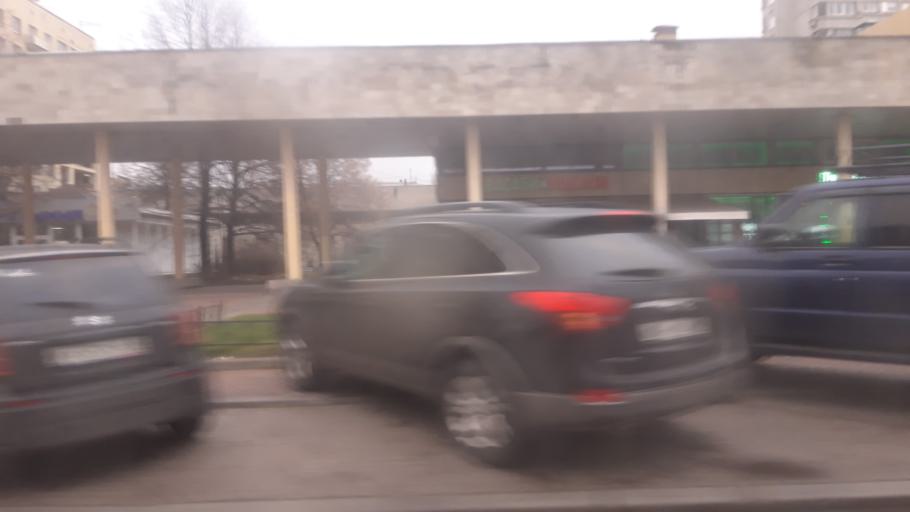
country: RU
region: St.-Petersburg
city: Kupchino
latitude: 59.8453
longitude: 30.3220
